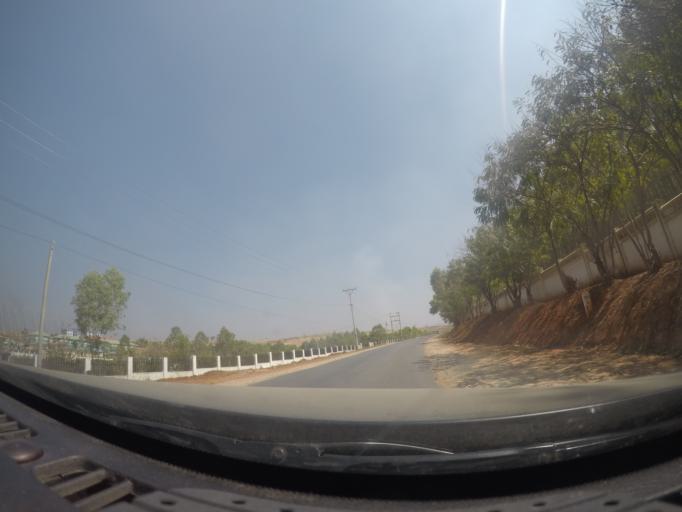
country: MM
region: Shan
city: Taunggyi
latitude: 20.8048
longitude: 97.1876
